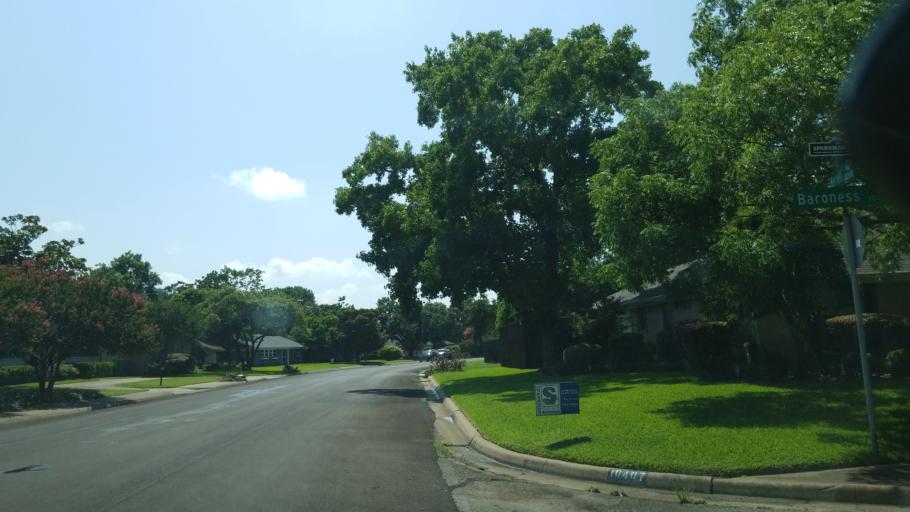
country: US
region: Texas
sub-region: Dallas County
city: Farmers Branch
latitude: 32.8874
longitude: -96.8677
